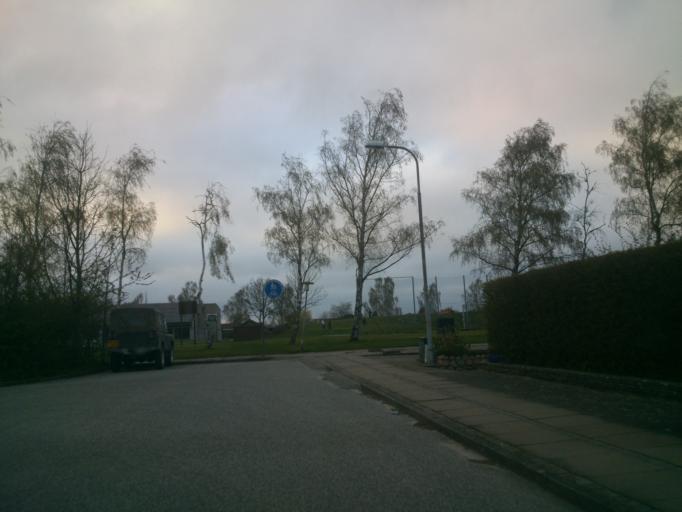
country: DK
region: South Denmark
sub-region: Fredericia Kommune
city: Fredericia
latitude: 55.5626
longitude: 9.7145
